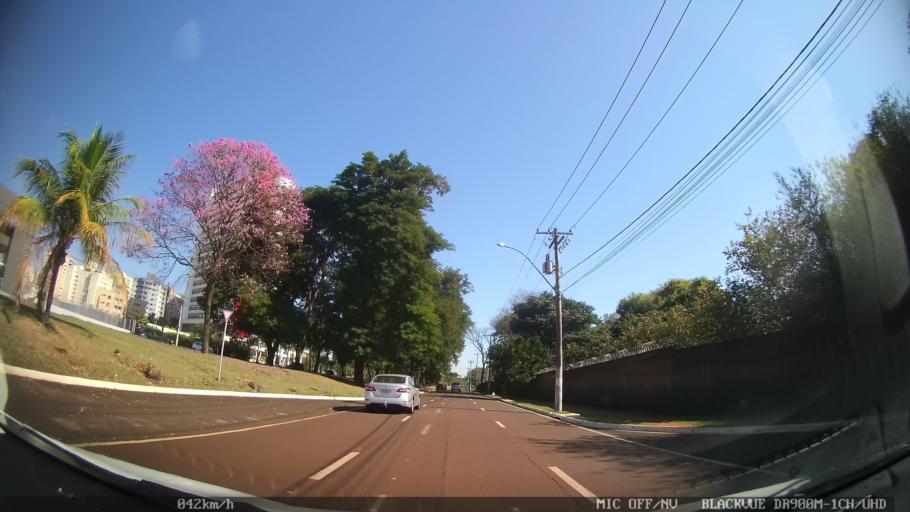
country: BR
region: Sao Paulo
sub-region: Ribeirao Preto
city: Ribeirao Preto
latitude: -21.2165
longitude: -47.8196
